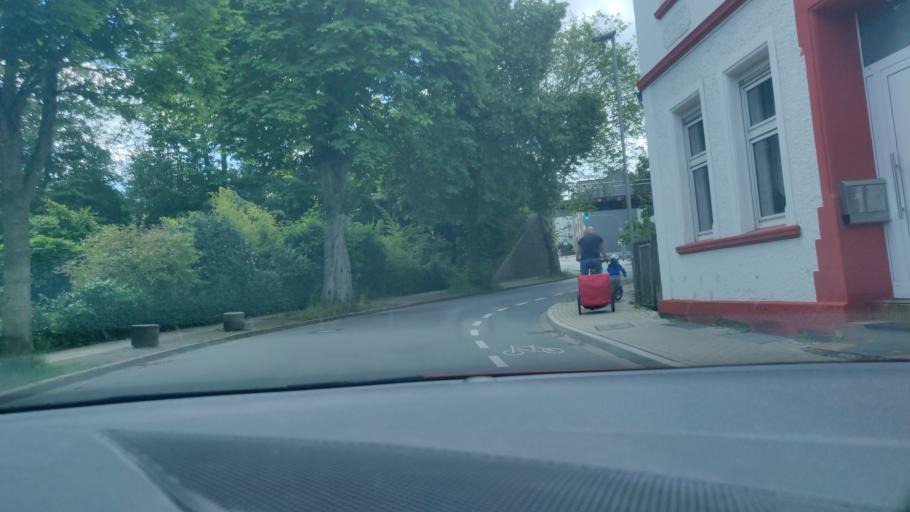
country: DE
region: North Rhine-Westphalia
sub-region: Regierungsbezirk Dusseldorf
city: Heiligenhaus
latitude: 51.3295
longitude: 6.9735
